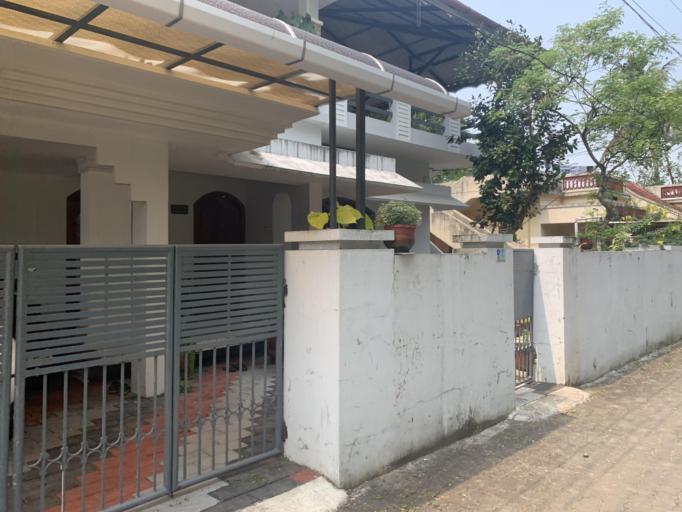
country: IN
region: Kerala
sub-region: Ernakulam
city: Cochin
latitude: 9.9436
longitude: 76.3064
